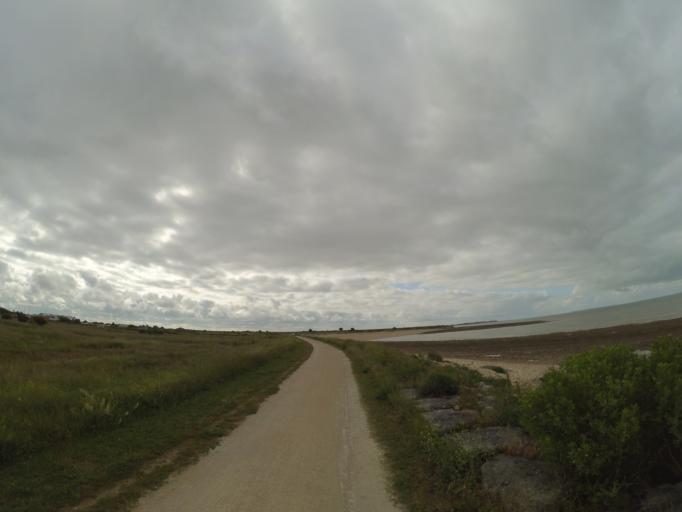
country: FR
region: Poitou-Charentes
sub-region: Departement de la Charente-Maritime
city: La Rochelle
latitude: 46.1344
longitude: -1.1510
